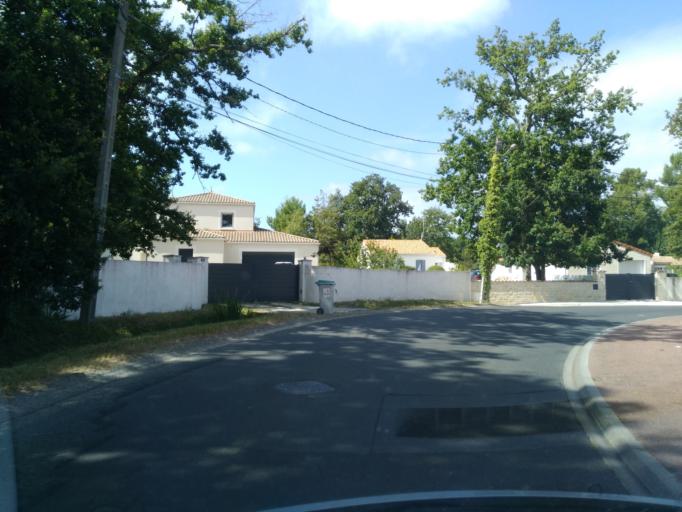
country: FR
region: Poitou-Charentes
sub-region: Departement de la Charente-Maritime
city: Breuillet
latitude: 45.6978
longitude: -1.0618
